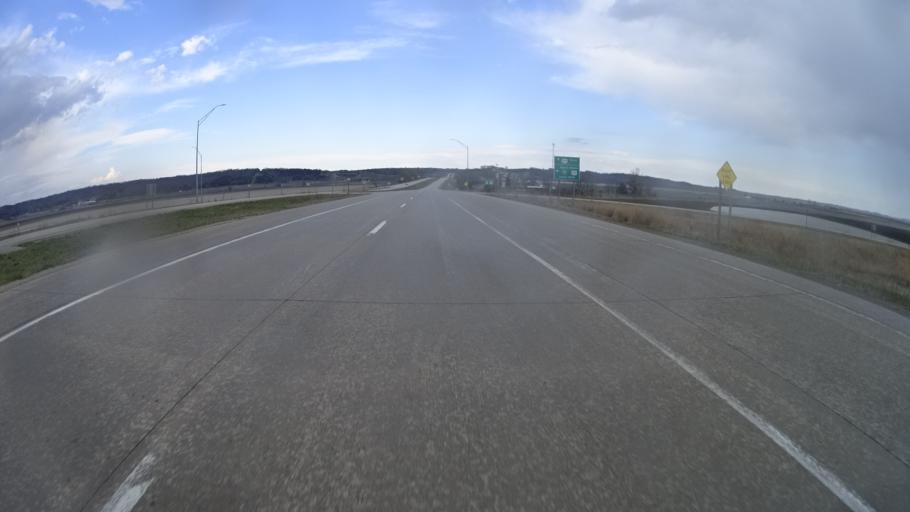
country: US
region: Nebraska
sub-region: Cass County
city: Plattsmouth
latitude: 41.0450
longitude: -95.8185
